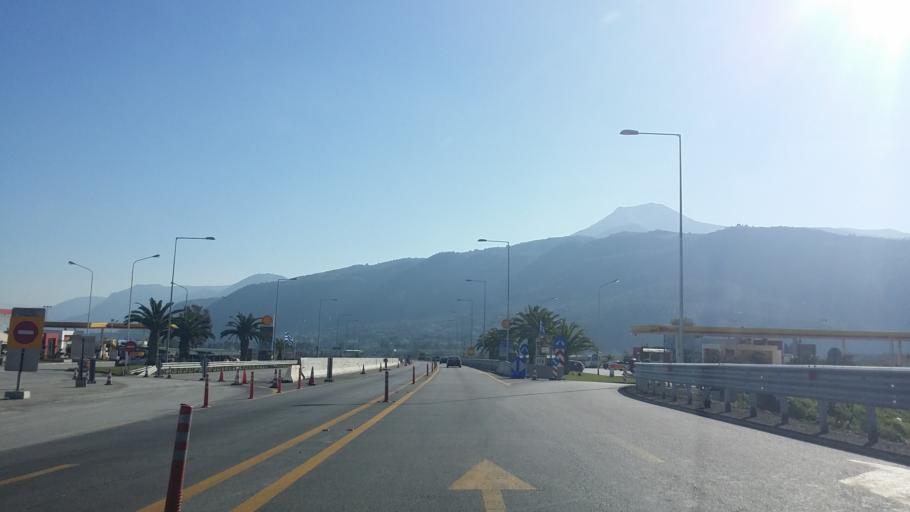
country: GR
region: West Greece
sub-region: Nomos Achaias
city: Aigio
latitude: 38.2362
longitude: 22.0782
